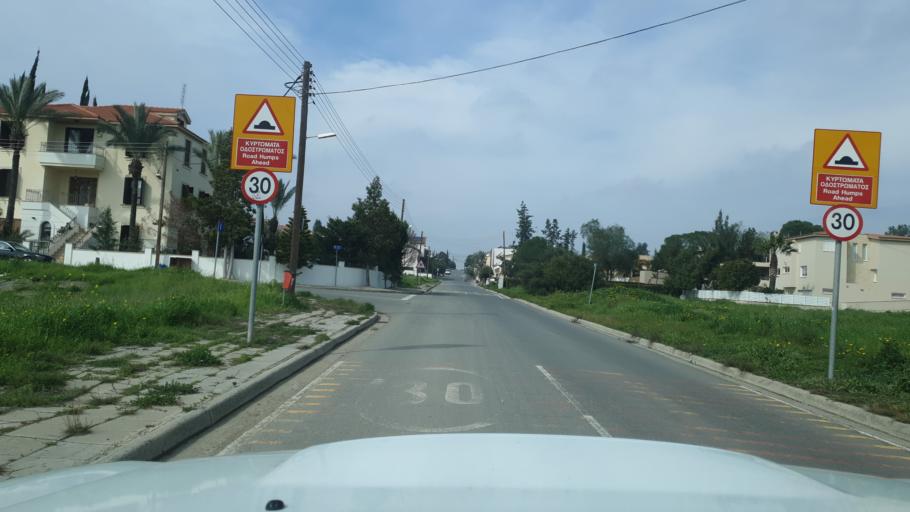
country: CY
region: Lefkosia
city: Tseri
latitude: 35.1184
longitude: 33.3497
